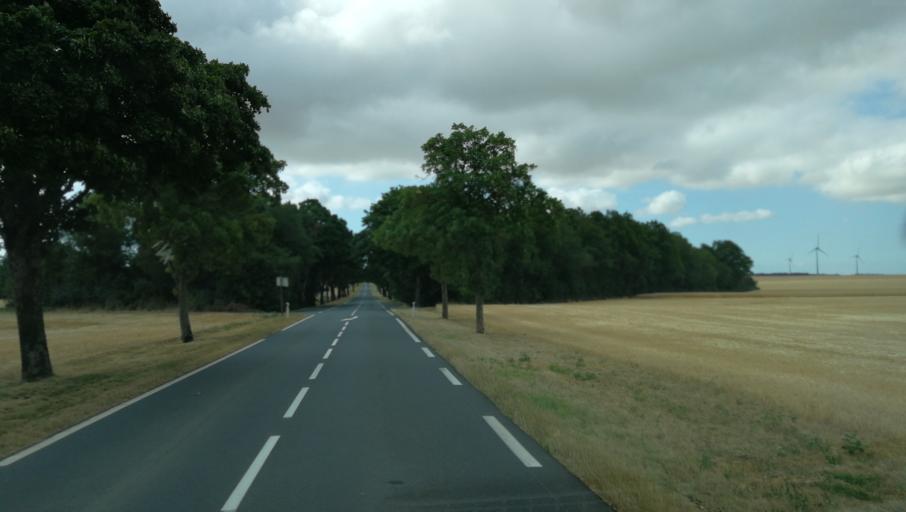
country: FR
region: Ile-de-France
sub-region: Departement de l'Essonne
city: Pussay
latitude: 48.4024
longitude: 1.9700
